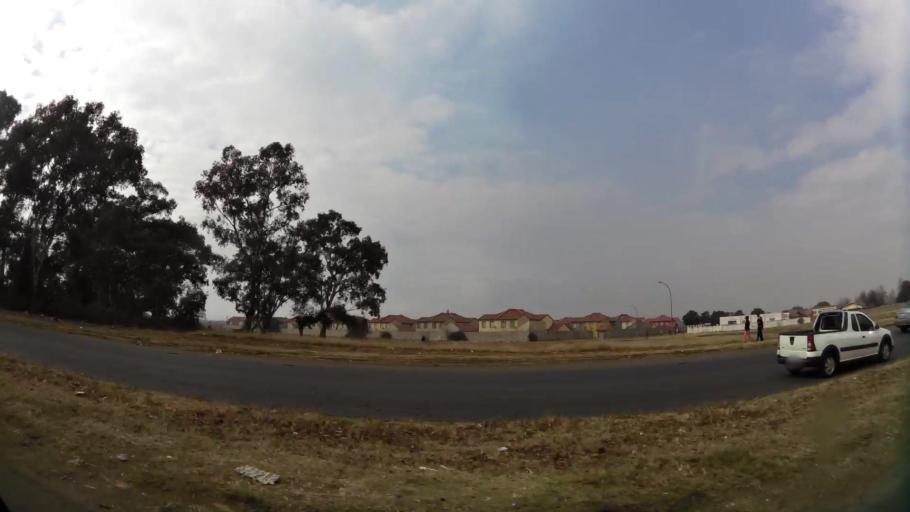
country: ZA
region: Gauteng
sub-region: Sedibeng District Municipality
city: Vanderbijlpark
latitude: -26.6784
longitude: 27.8380
